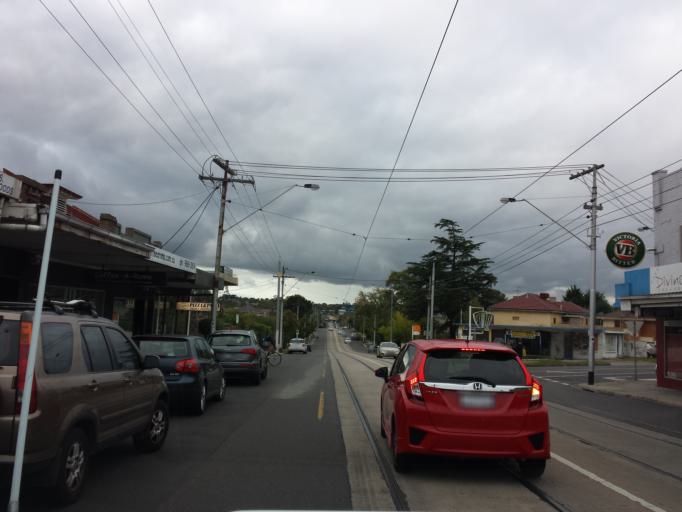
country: AU
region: Victoria
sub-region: Boroondara
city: Camberwell
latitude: -37.8423
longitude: 145.0693
